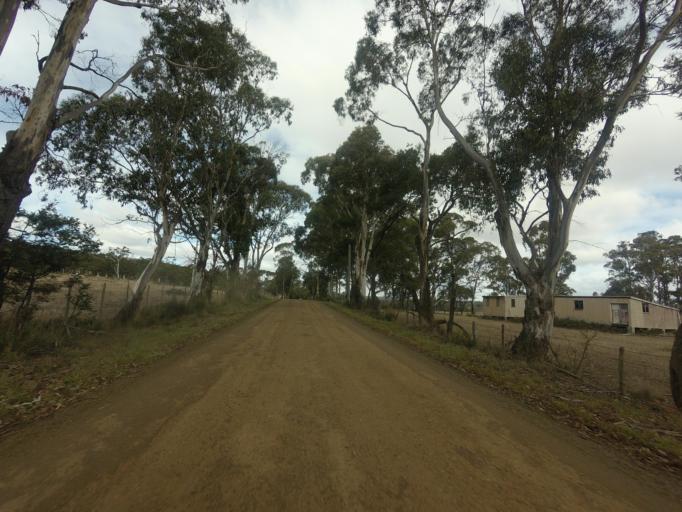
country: AU
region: Tasmania
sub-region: Brighton
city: Bridgewater
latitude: -42.4231
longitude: 147.4249
